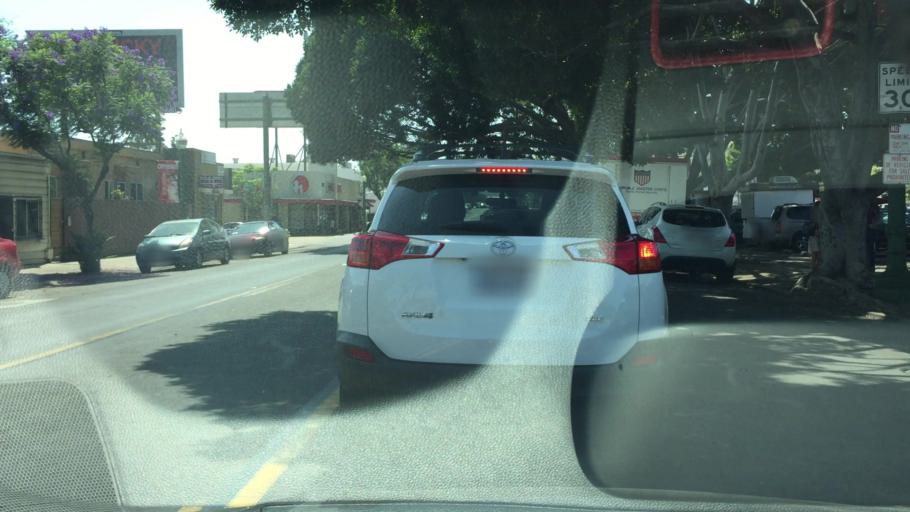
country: US
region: California
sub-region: San Diego County
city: San Diego
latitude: 32.7498
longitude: -117.1113
